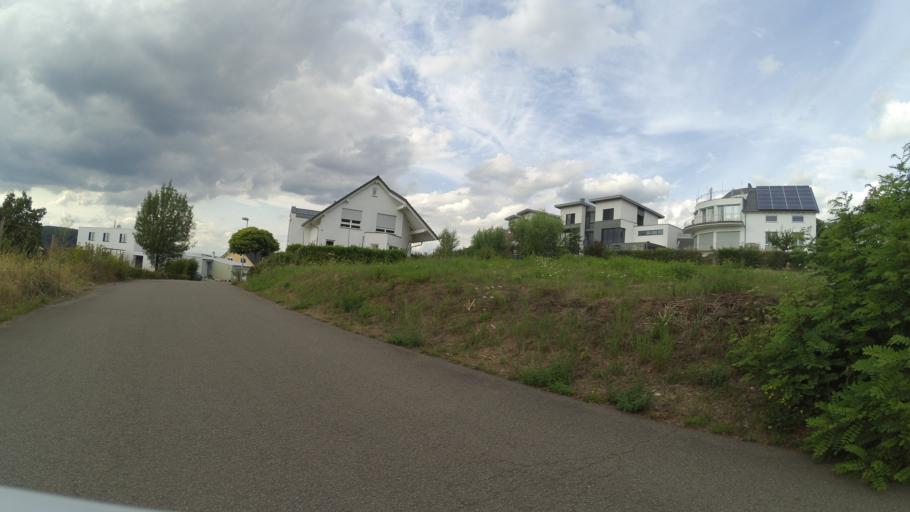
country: DE
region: Rheinland-Pfalz
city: Zweibrucken
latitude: 49.2705
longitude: 7.3252
